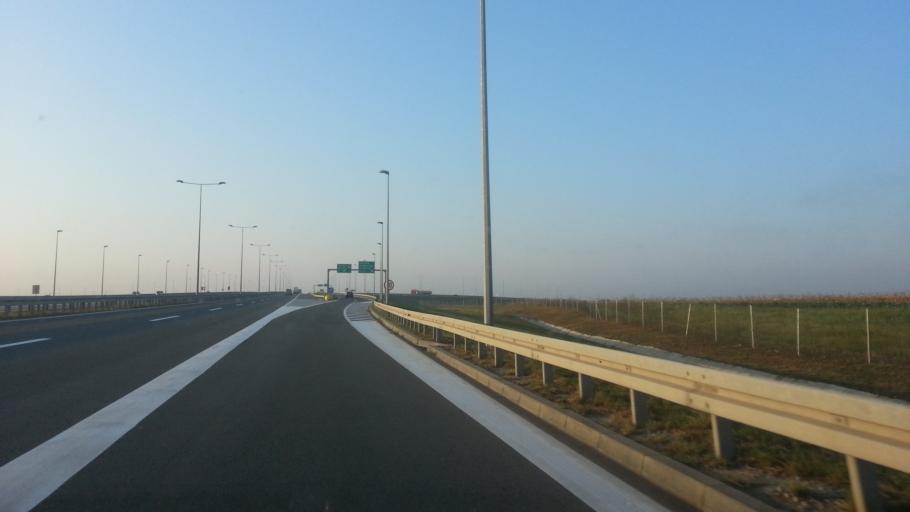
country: RS
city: Dobanovci
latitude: 44.8417
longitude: 20.2501
